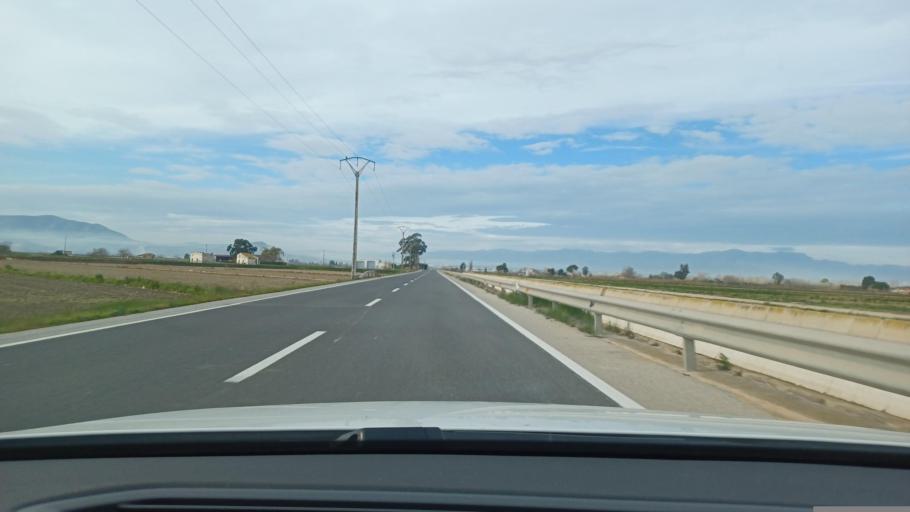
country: ES
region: Catalonia
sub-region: Provincia de Tarragona
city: Deltebre
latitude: 40.7106
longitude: 0.6650
